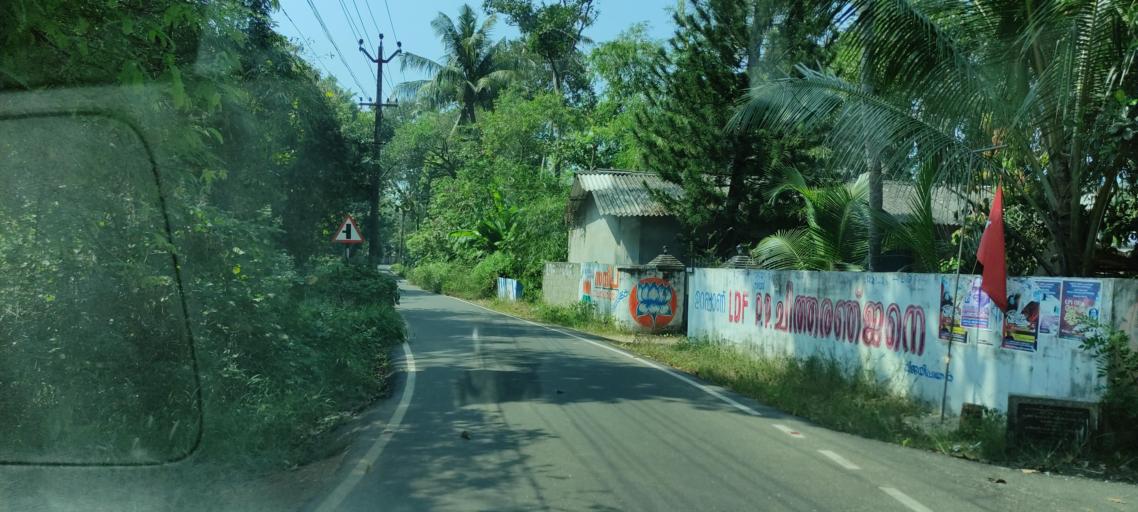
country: IN
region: Kerala
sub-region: Alappuzha
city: Alleppey
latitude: 9.5552
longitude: 76.3147
